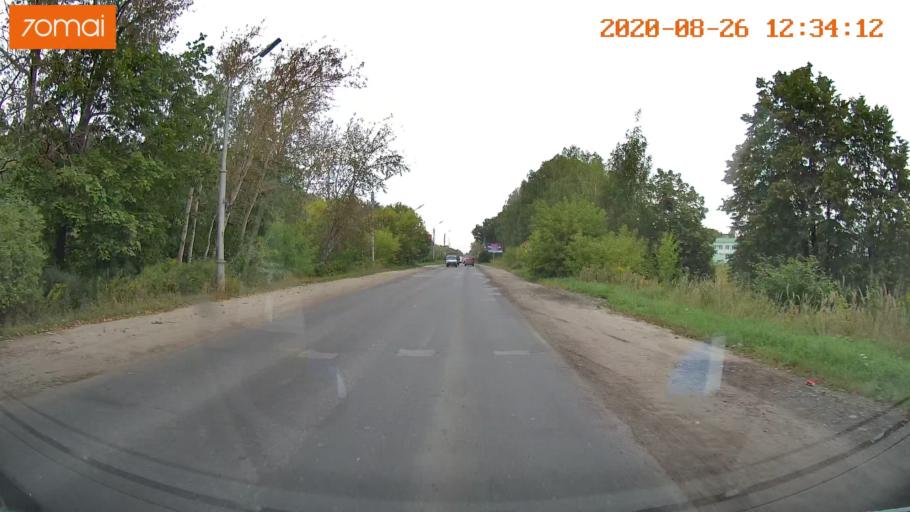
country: RU
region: Rjazan
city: Ryazan'
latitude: 54.5866
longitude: 39.7721
